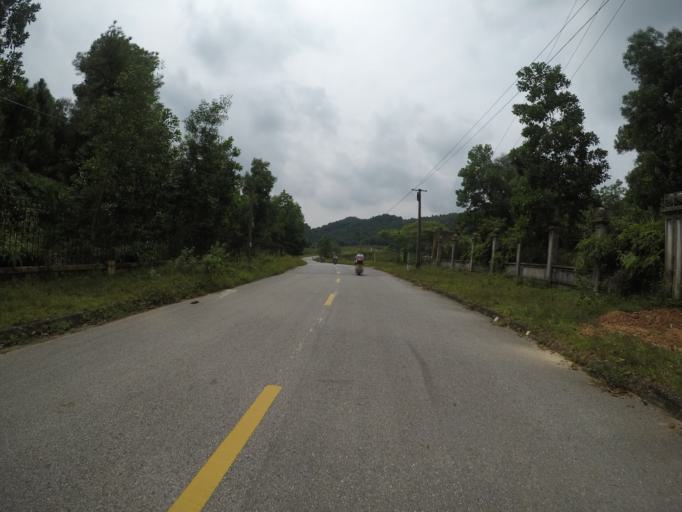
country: VN
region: Ha Noi
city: Soc Son
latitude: 21.2842
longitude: 105.8322
